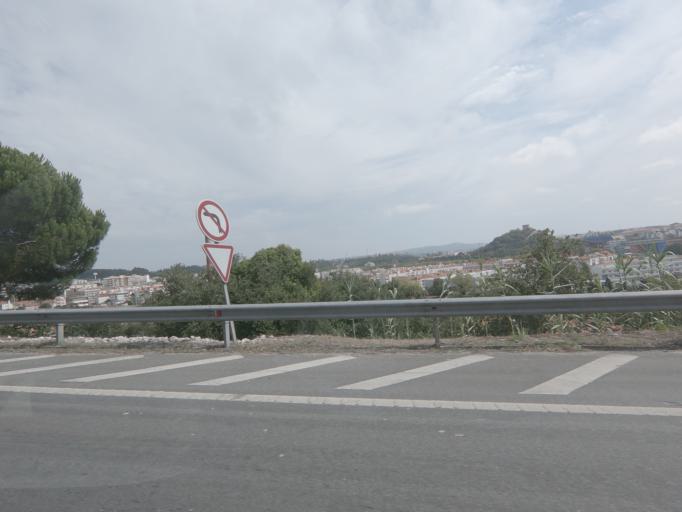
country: PT
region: Leiria
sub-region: Leiria
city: Leiria
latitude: 39.7565
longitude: -8.8134
